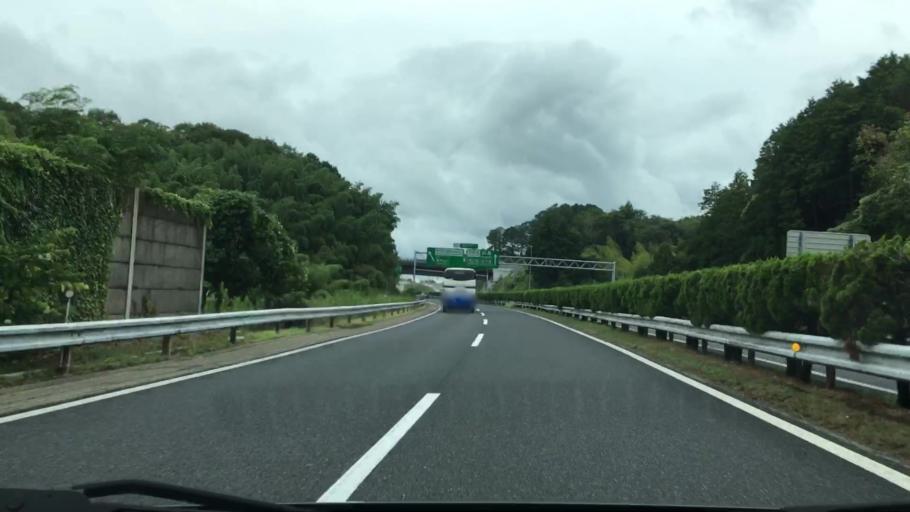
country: JP
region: Okayama
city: Tsuyama
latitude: 35.0344
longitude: 134.1436
